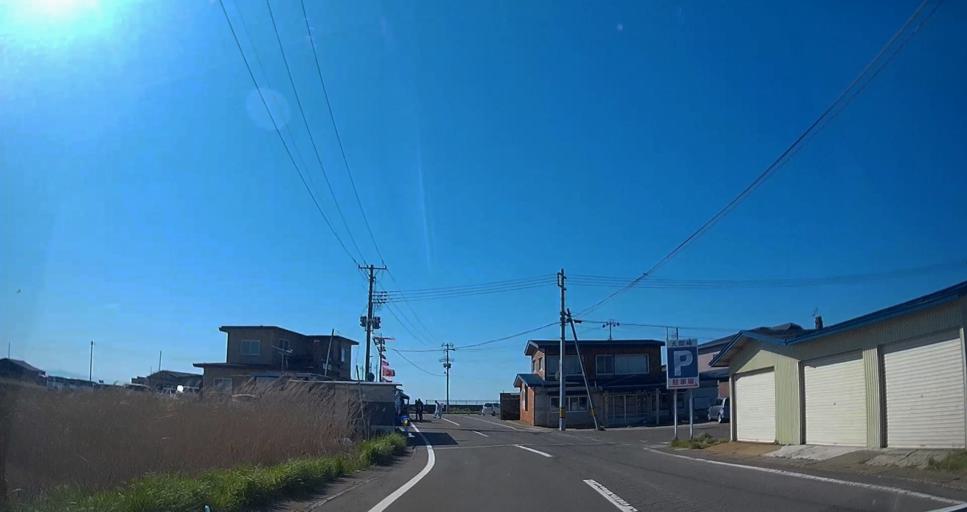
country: JP
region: Hokkaido
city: Hakodate
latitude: 41.5452
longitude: 140.9131
